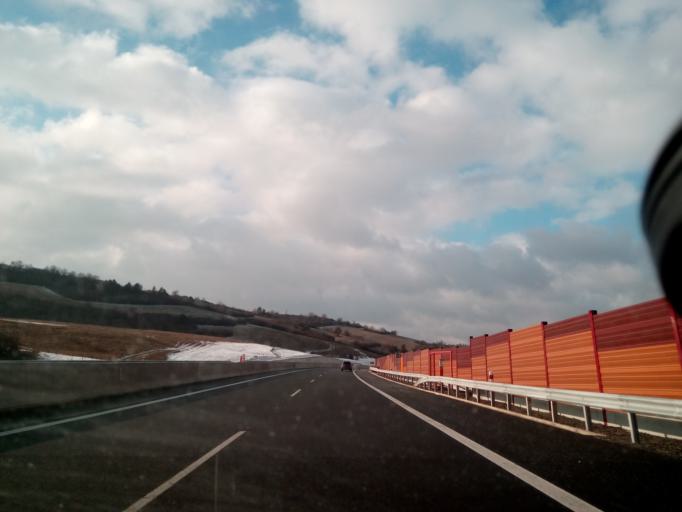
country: SK
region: Presovsky
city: Sabinov
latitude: 48.9986
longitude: 21.0739
